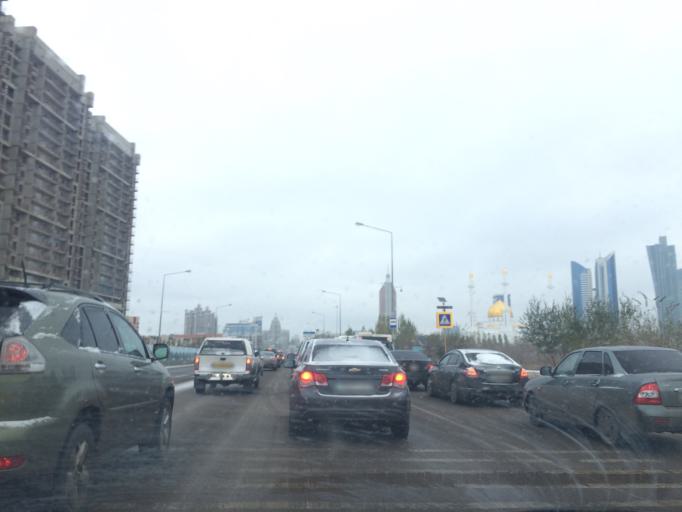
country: KZ
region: Astana Qalasy
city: Astana
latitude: 51.1228
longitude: 71.4126
